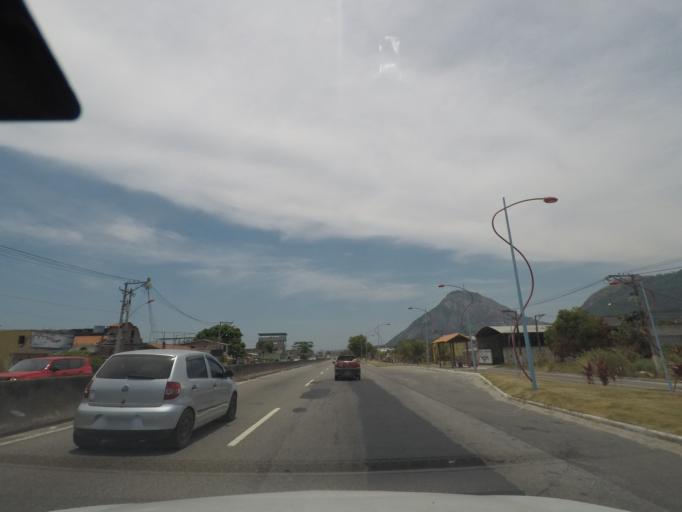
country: BR
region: Rio de Janeiro
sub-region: Marica
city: Marica
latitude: -22.9317
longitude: -42.8831
